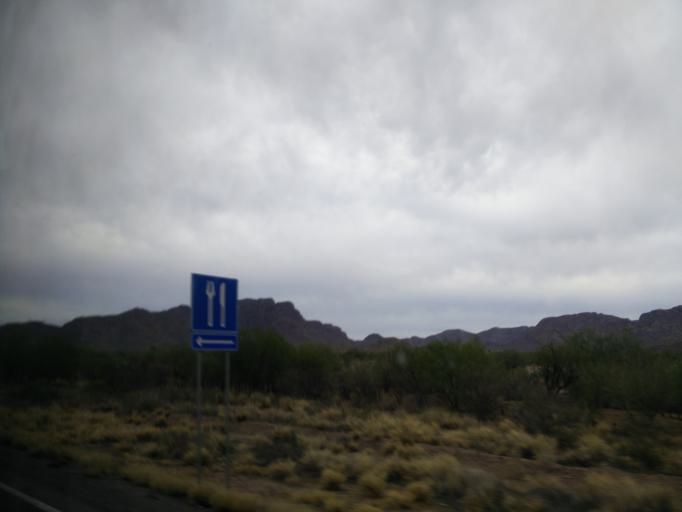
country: MX
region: Sonora
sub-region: Hermosillo
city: Miguel Aleman (La Doce)
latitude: 28.5838
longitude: -111.0270
